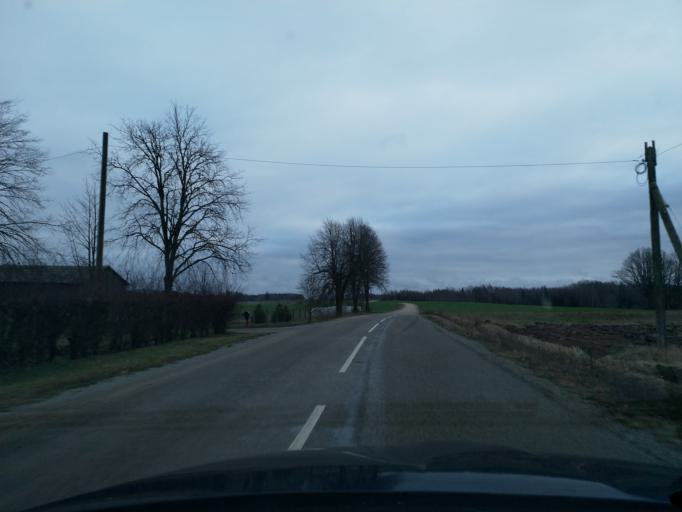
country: LV
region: Kuldigas Rajons
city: Kuldiga
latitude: 56.8947
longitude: 22.2590
